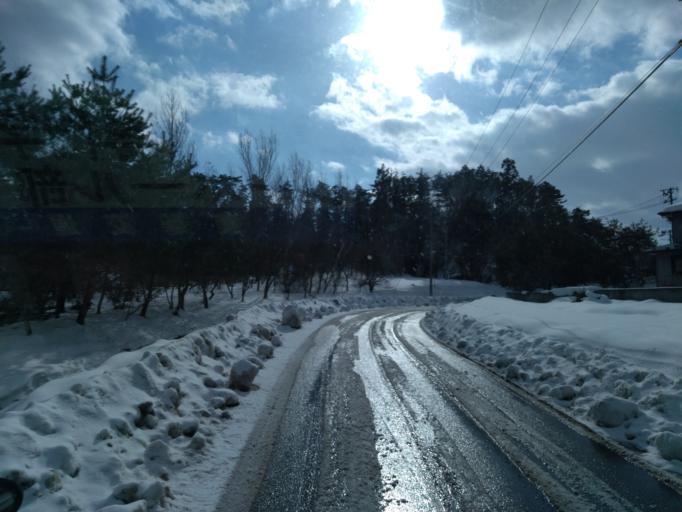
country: JP
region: Iwate
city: Mizusawa
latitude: 39.1310
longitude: 141.1942
